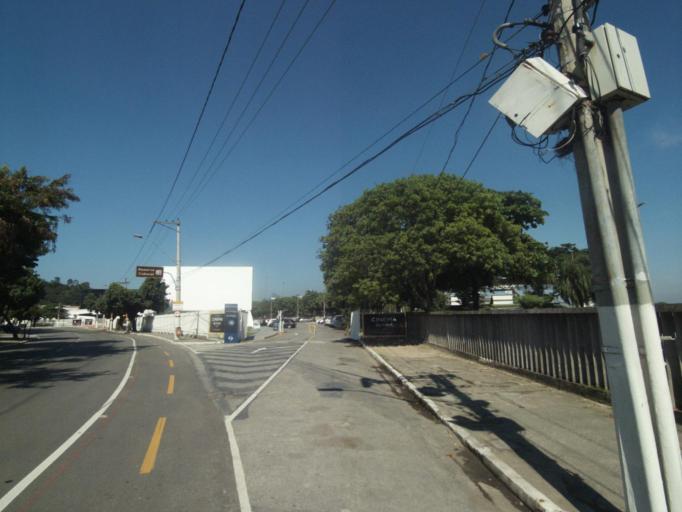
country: BR
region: Rio de Janeiro
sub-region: Niteroi
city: Niteroi
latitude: -22.8971
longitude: -43.1298
